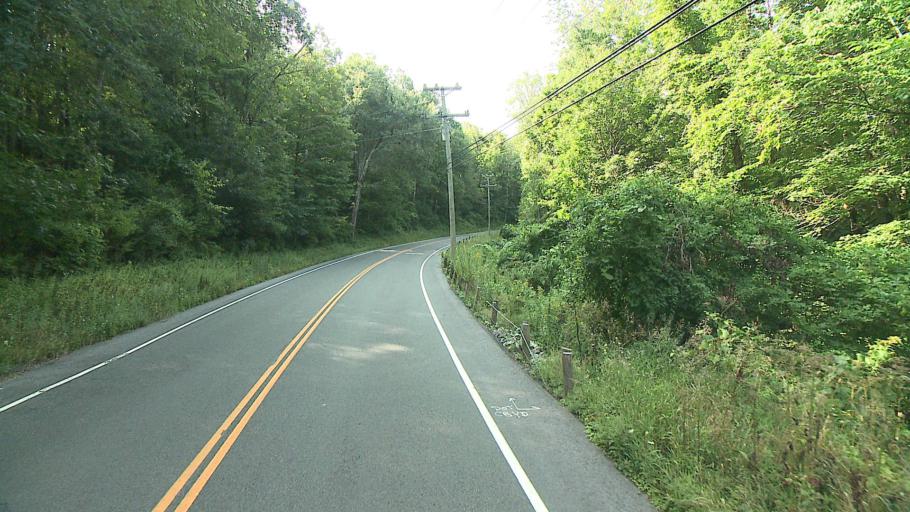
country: US
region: Connecticut
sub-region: Litchfield County
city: Kent
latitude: 41.7735
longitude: -73.4194
